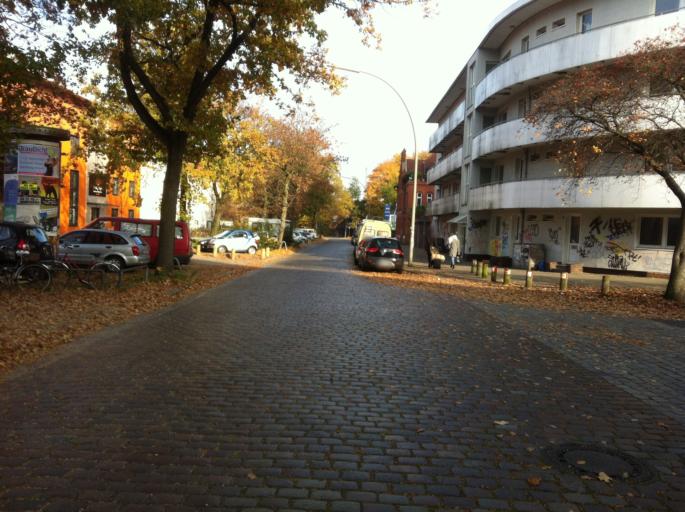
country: DE
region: Hamburg
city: Altona
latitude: 53.5645
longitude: 9.9295
